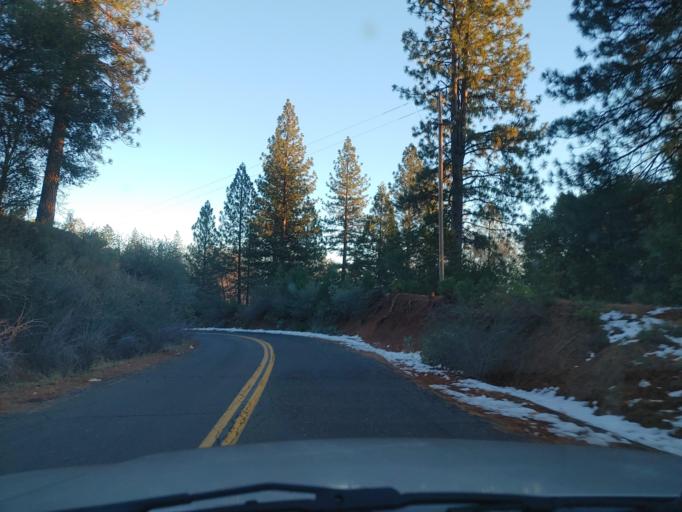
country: US
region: California
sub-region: Tuolumne County
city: Cedar Ridge
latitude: 38.0421
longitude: -120.2910
